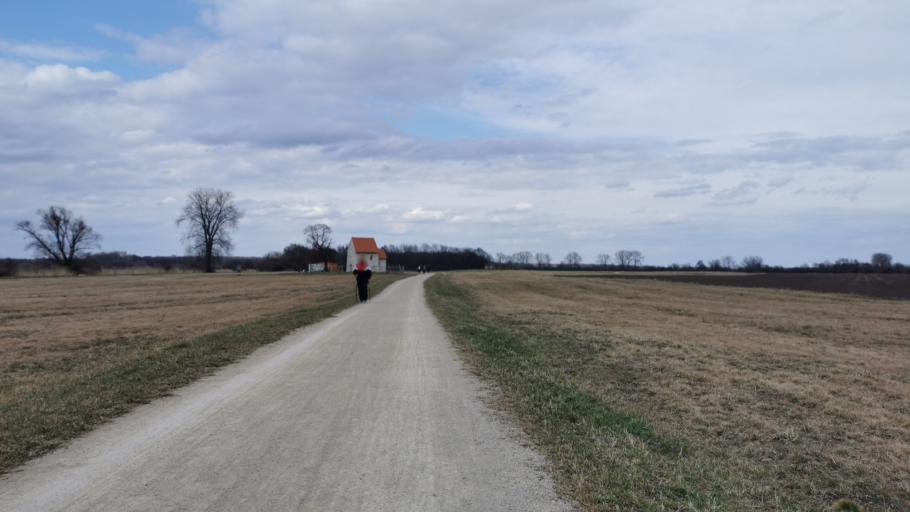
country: SK
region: Trnavsky
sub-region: Okres Skalica
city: Holic
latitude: 48.7949
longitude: 17.1074
